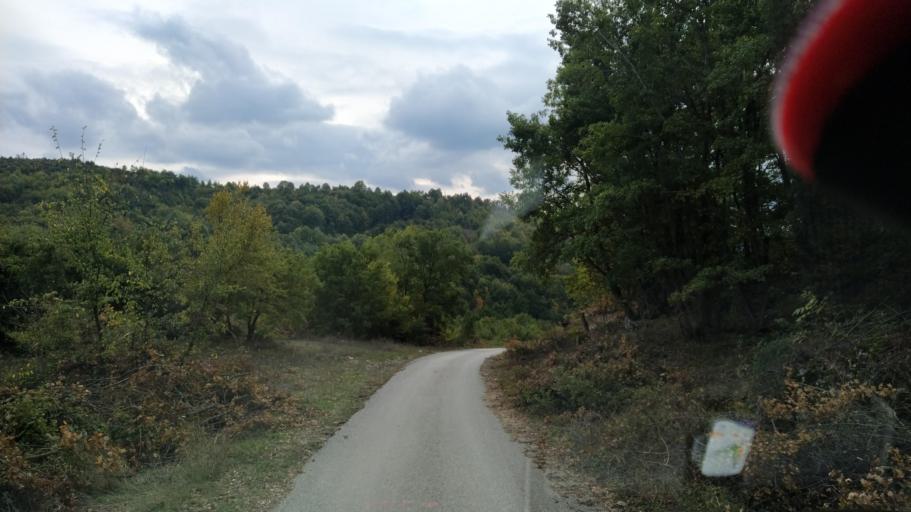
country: MK
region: Strumica
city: Veljusa
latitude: 41.5113
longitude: 22.4888
